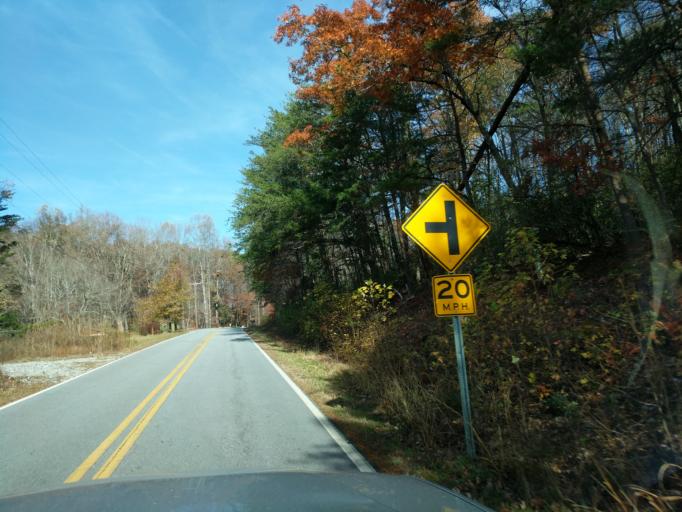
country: US
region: North Carolina
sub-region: Polk County
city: Columbus
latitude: 35.2600
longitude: -82.2065
